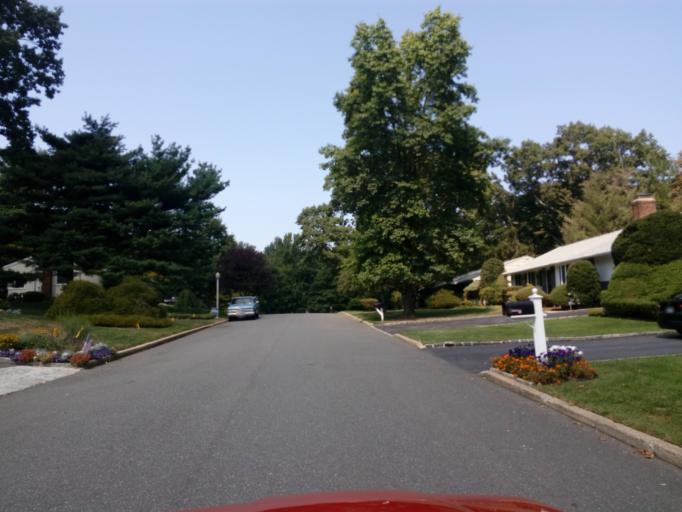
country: US
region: New York
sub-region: Nassau County
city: Glen Cove
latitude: 40.8770
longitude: -73.6375
